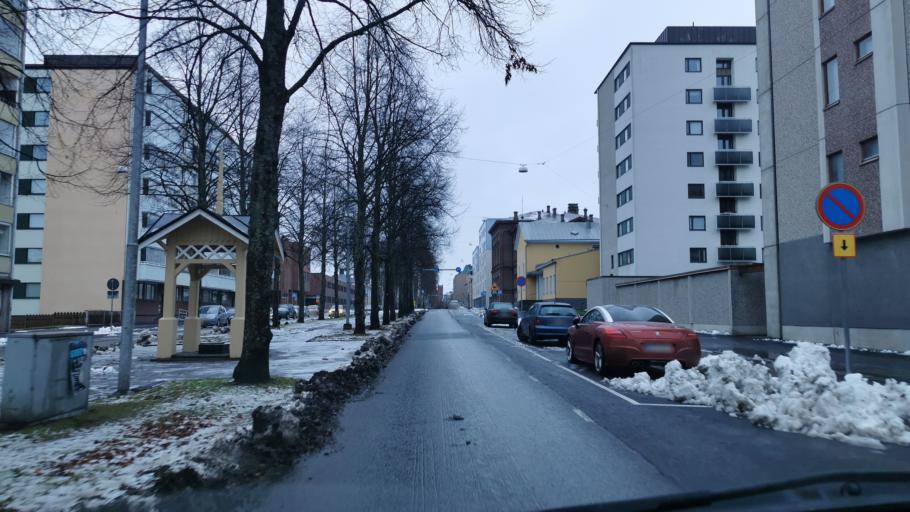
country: FI
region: Ostrobothnia
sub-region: Vaasa
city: Vaasa
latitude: 63.0992
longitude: 21.6060
